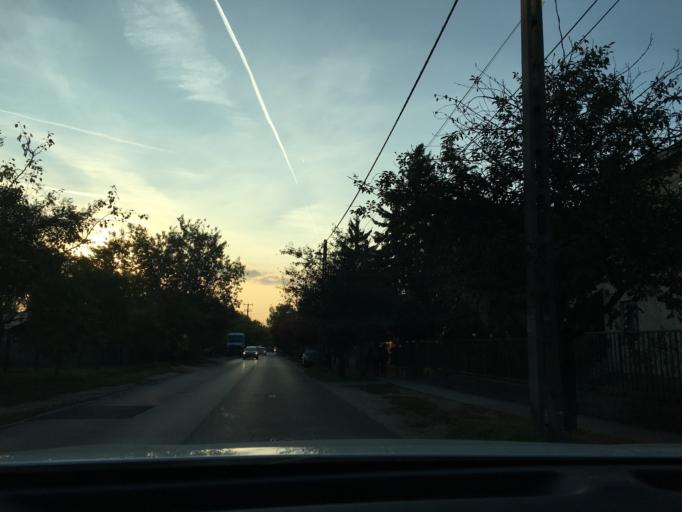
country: HU
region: Budapest
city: Budapest XVII. keruelet
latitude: 47.4753
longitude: 19.2507
